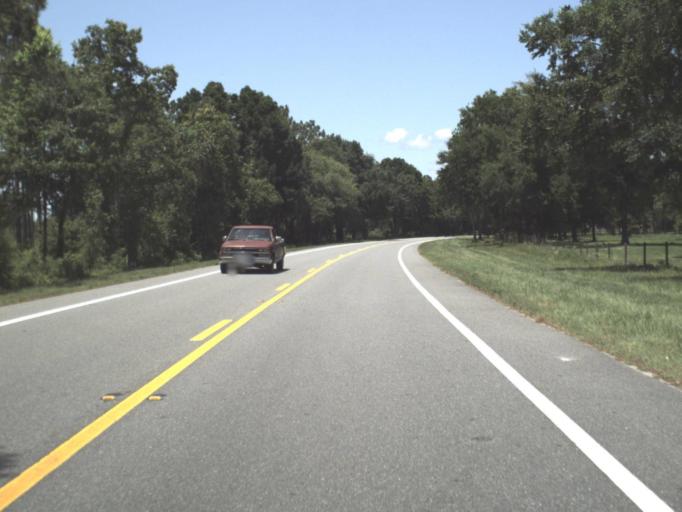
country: US
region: Florida
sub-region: Dixie County
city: Cross City
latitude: 29.8368
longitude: -82.9685
